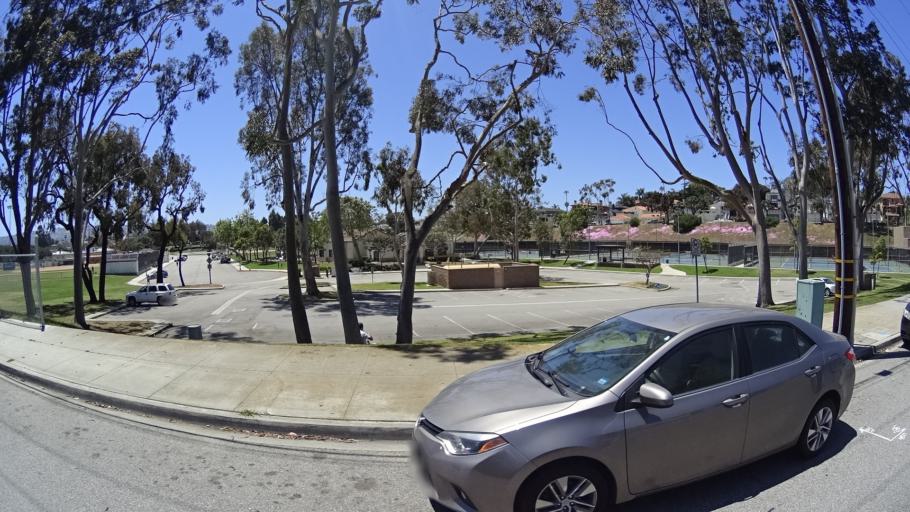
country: US
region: California
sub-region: Los Angeles County
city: Redondo Beach
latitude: 33.8319
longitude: -118.3784
